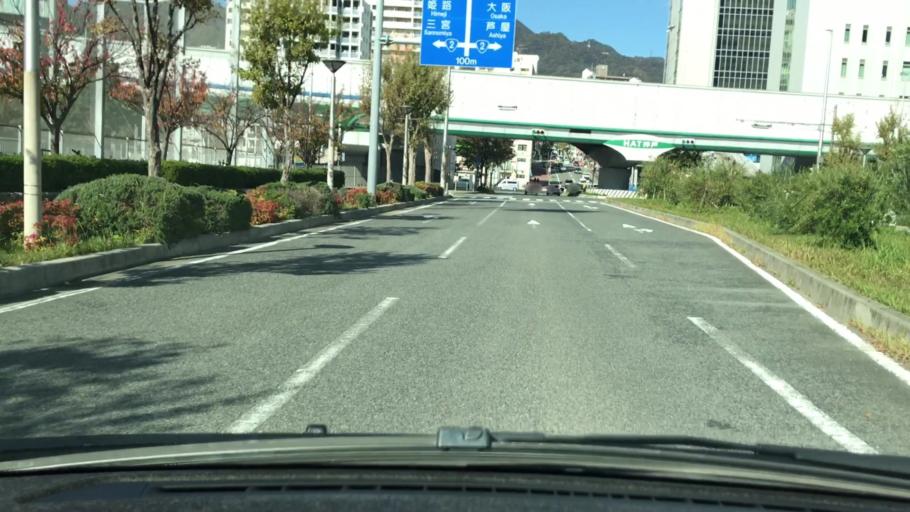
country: JP
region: Hyogo
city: Kobe
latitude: 34.7011
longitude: 135.2178
